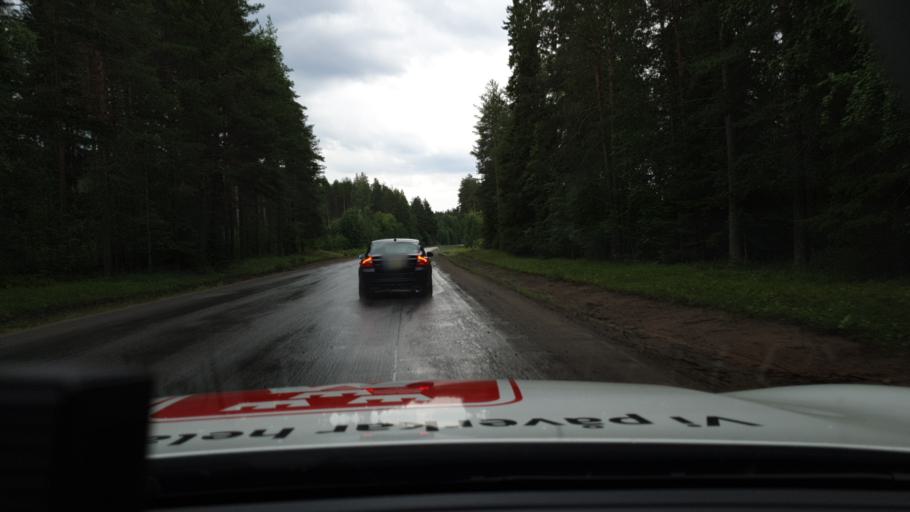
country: SE
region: Norrbotten
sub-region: Bodens Kommun
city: Boden
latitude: 65.8783
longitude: 21.4059
